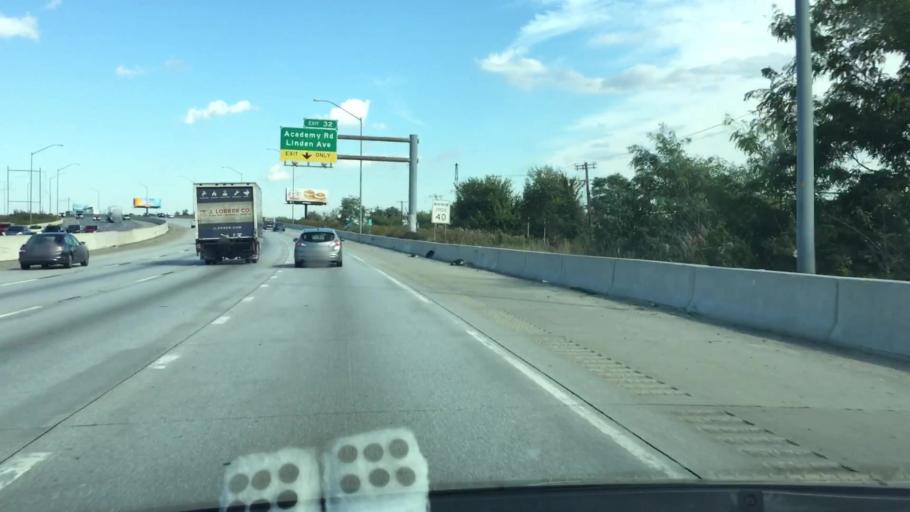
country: US
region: New Jersey
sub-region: Burlington County
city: Riverton
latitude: 40.0390
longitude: -75.0078
